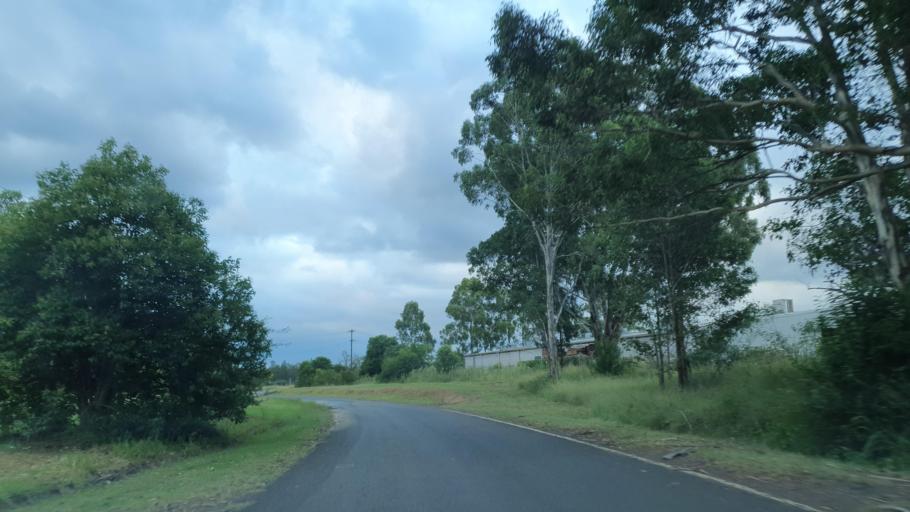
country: AU
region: New South Wales
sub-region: Penrith Municipality
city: Werrington County
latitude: -33.7417
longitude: 150.7629
